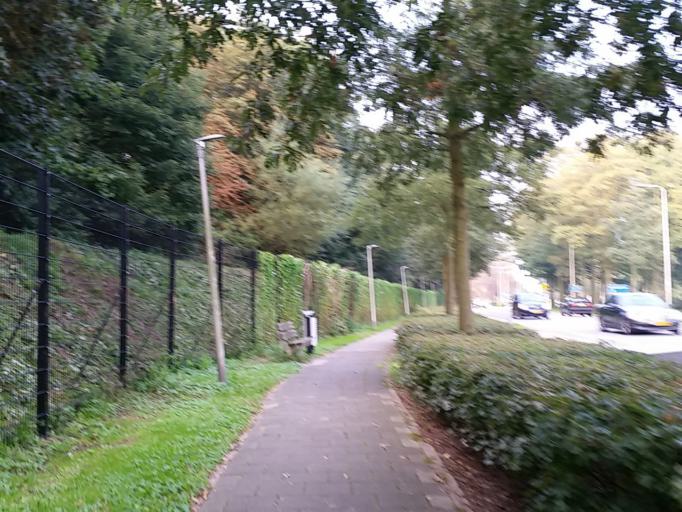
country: NL
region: South Holland
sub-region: Gemeente Noordwijk
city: Noordwijk-Binnen
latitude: 52.2360
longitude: 4.4533
